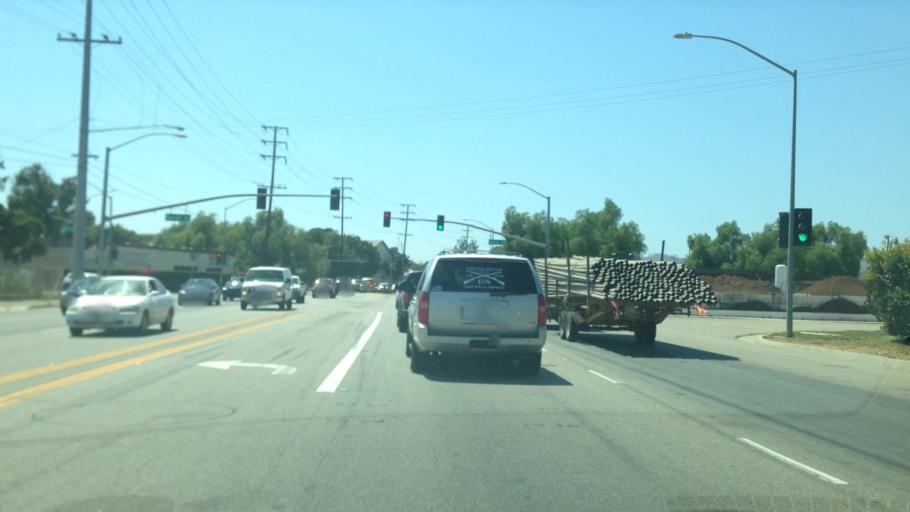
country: US
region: California
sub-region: Ventura County
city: Saticoy
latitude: 34.2820
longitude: -119.1469
